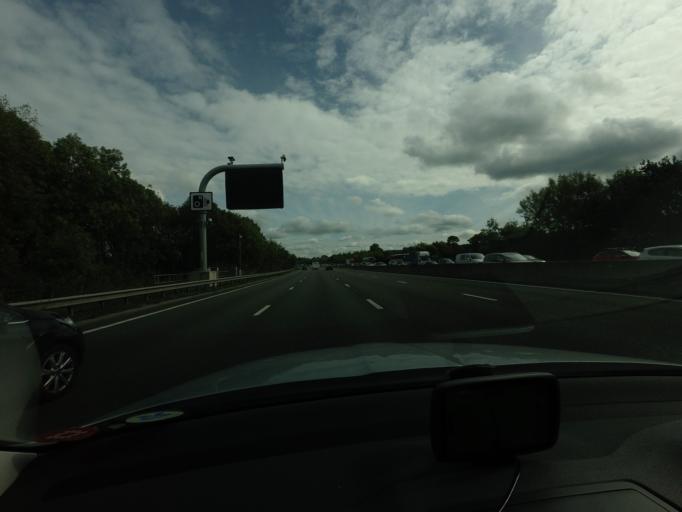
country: GB
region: England
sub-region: Surrey
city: Oxted
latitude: 51.2677
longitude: 0.0139
